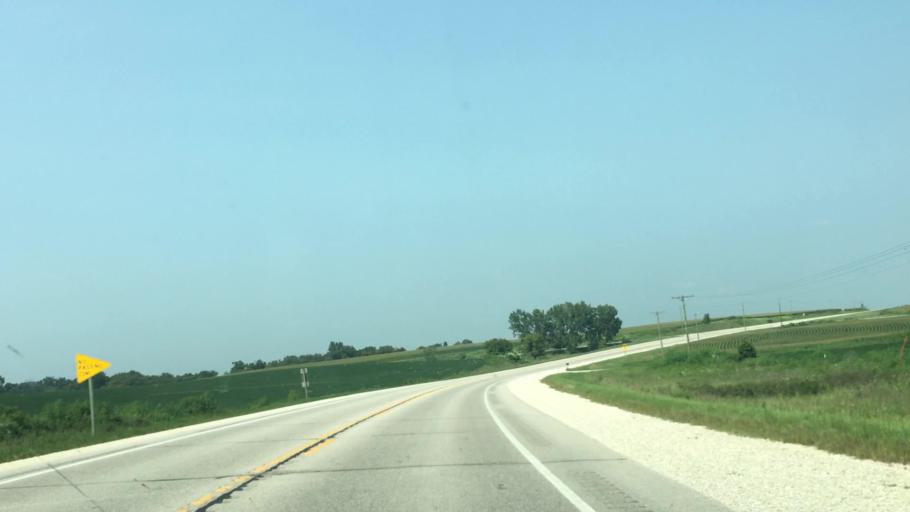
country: US
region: Iowa
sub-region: Winneshiek County
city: Decorah
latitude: 43.2086
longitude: -91.8791
